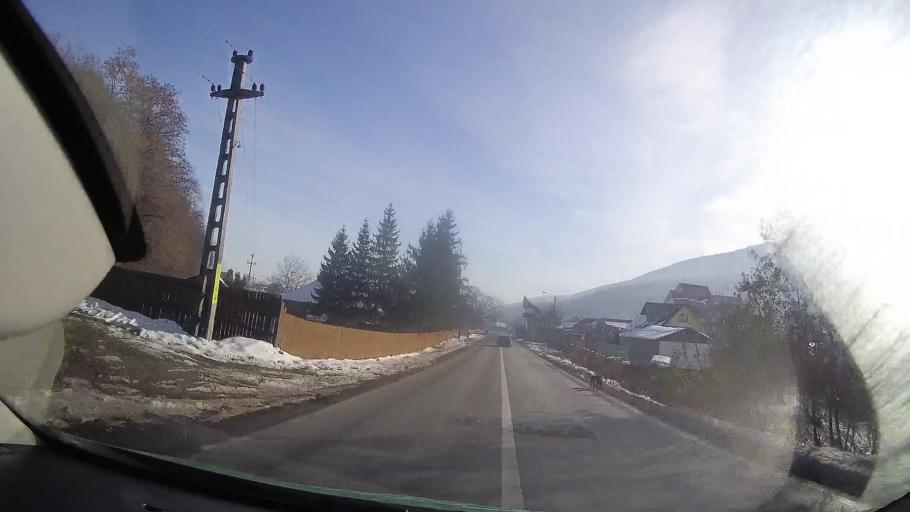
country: RO
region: Neamt
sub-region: Comuna Garcina
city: Garcina
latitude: 46.9754
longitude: 26.3617
